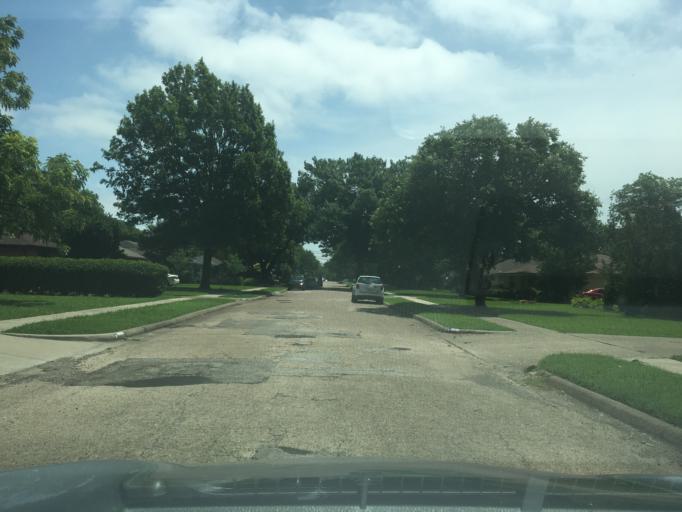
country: US
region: Texas
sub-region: Dallas County
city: Richardson
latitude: 32.9472
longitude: -96.7454
